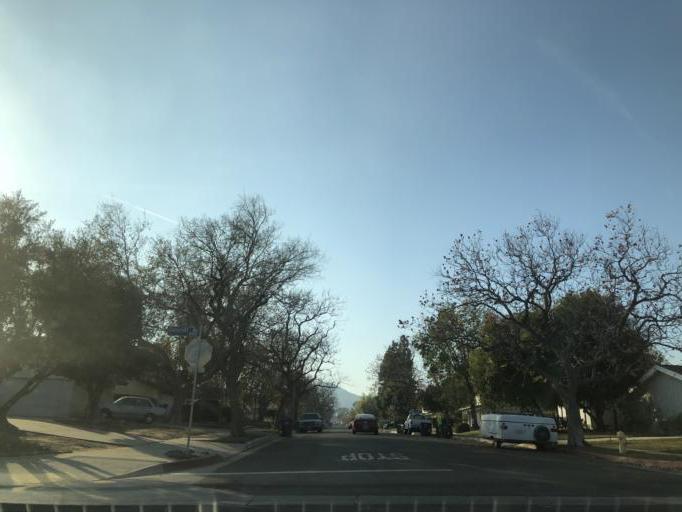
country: US
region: California
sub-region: Los Angeles County
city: Chatsworth
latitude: 34.2607
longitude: -118.5819
